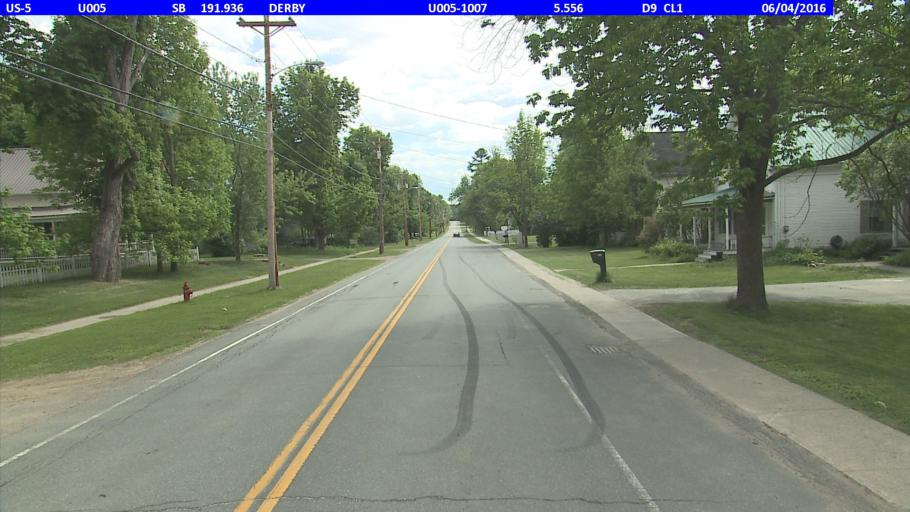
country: US
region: Vermont
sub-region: Orleans County
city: Newport
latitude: 45.0008
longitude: -72.1028
